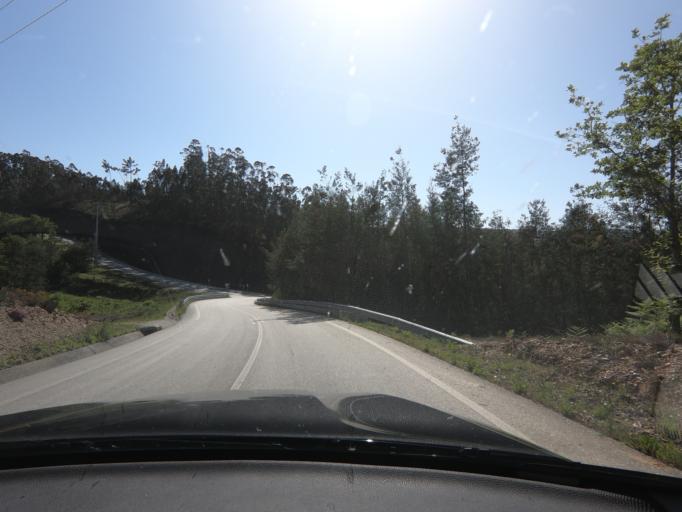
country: PT
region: Coimbra
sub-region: Penacova
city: Penacova
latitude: 40.2932
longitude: -8.2518
